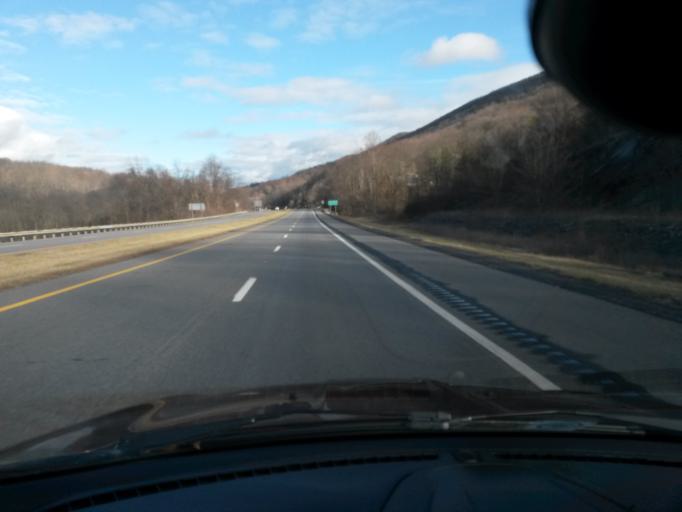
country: US
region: West Virginia
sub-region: Mercer County
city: Bluefield
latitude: 37.2758
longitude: -81.1525
